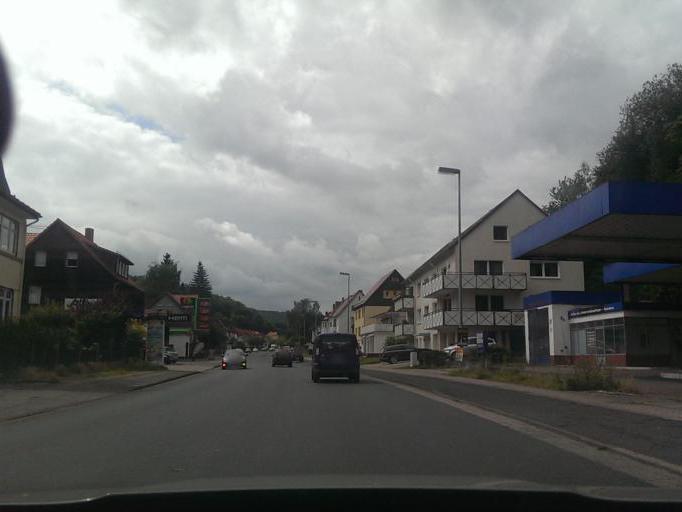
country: DE
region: Lower Saxony
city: Alfeld
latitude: 51.9773
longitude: 9.8151
